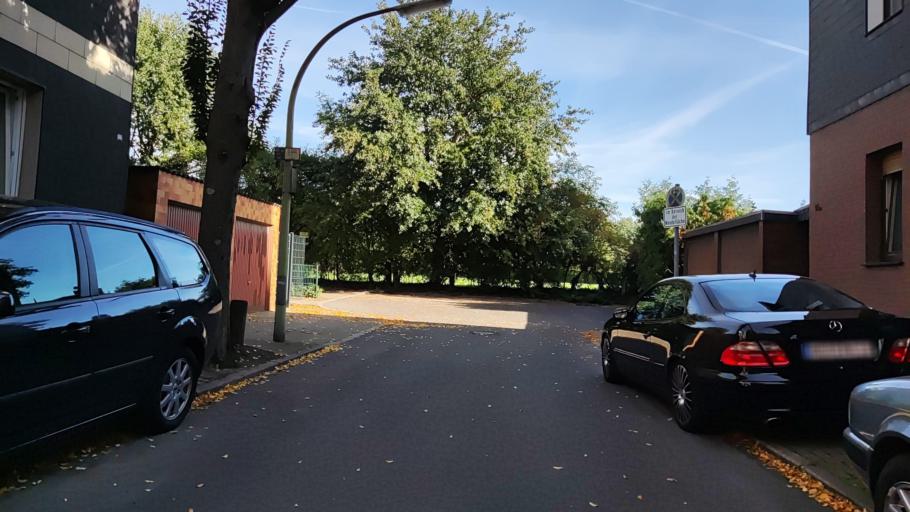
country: DE
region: North Rhine-Westphalia
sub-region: Regierungsbezirk Arnsberg
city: Herne
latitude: 51.5564
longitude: 7.2191
